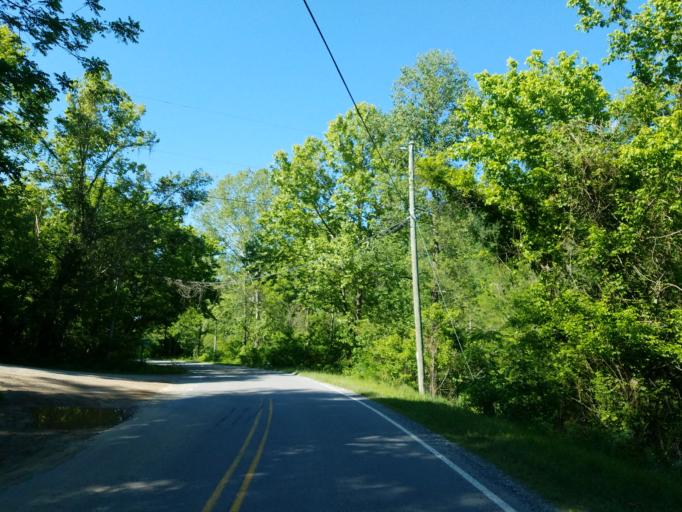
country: US
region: Georgia
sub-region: Pickens County
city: Jasper
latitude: 34.5532
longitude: -84.5101
